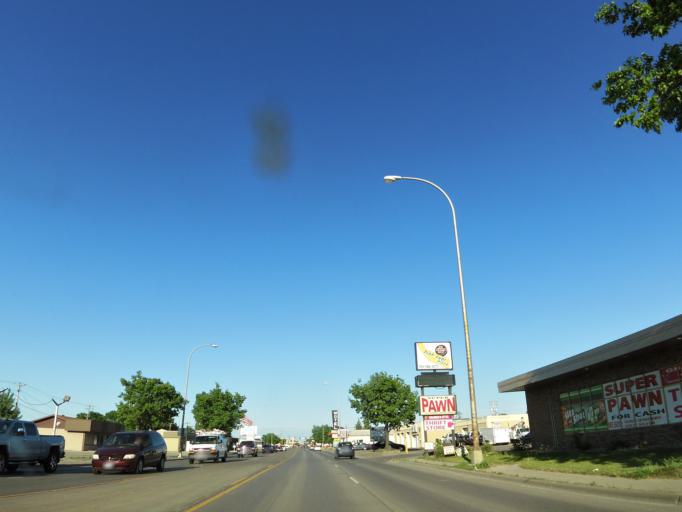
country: US
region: North Dakota
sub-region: Grand Forks County
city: Grand Forks
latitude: 47.9331
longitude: -97.0599
